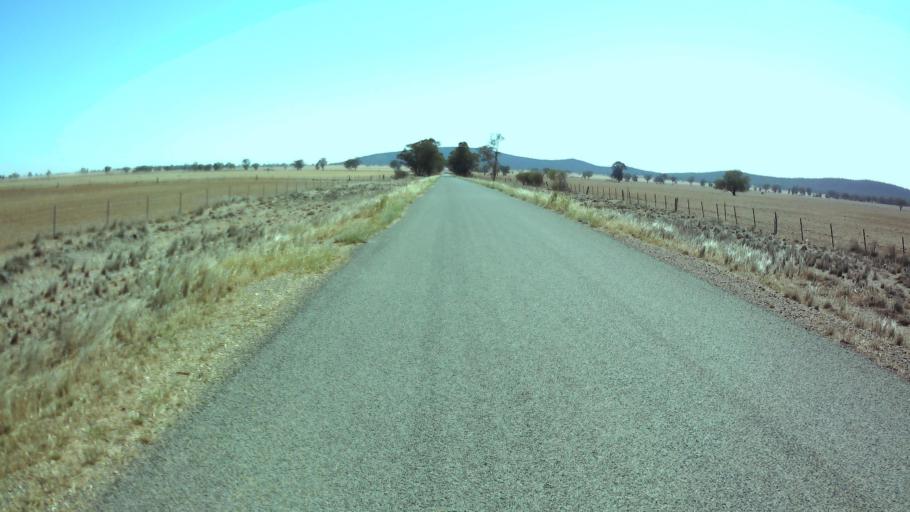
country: AU
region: New South Wales
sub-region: Weddin
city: Grenfell
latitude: -33.7119
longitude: 147.9103
